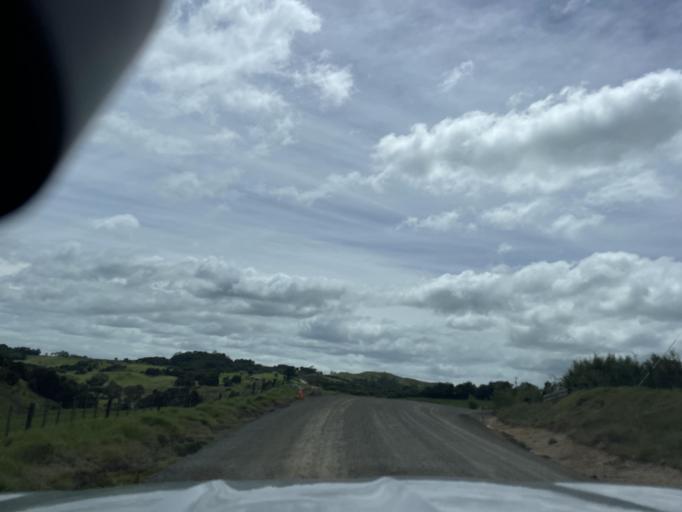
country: NZ
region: Auckland
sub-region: Auckland
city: Wellsford
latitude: -36.1633
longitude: 174.2835
